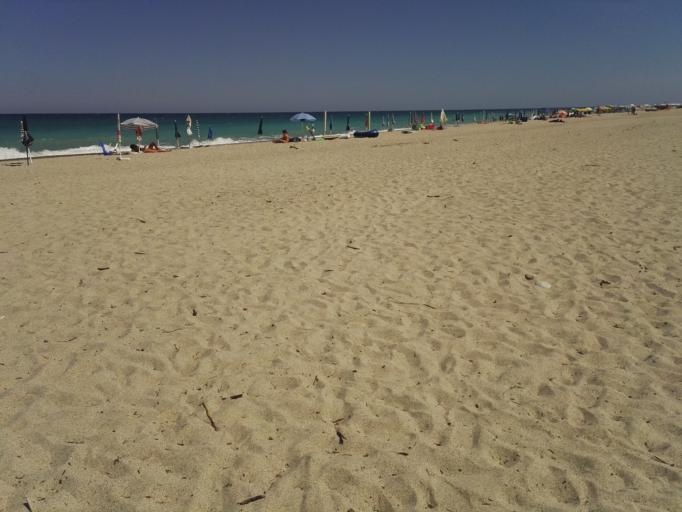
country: IT
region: Calabria
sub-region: Provincia di Catanzaro
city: Santa Caterina dello Ionio Marina
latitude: 38.5290
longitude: 16.5725
